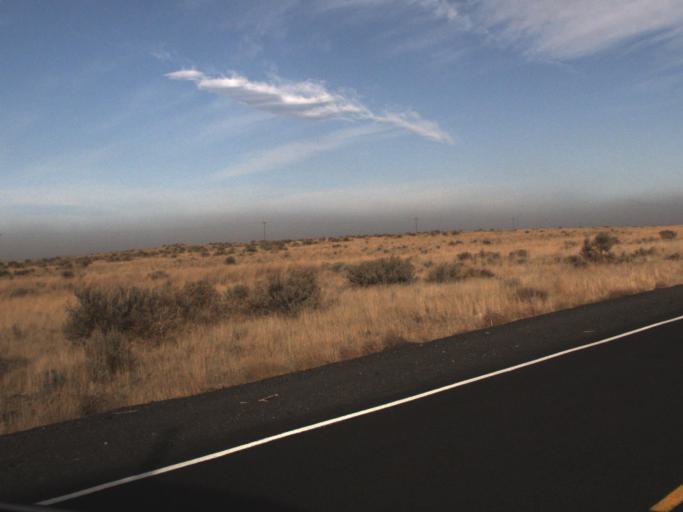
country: US
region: Washington
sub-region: Grant County
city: Warden
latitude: 47.3176
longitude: -118.8425
